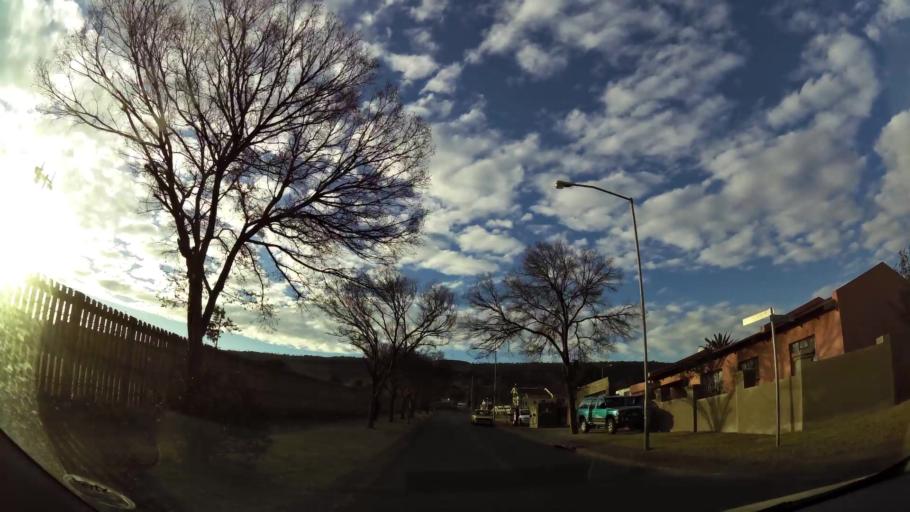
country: ZA
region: Gauteng
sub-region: City of Tshwane Metropolitan Municipality
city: Pretoria
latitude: -25.7021
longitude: 28.3156
